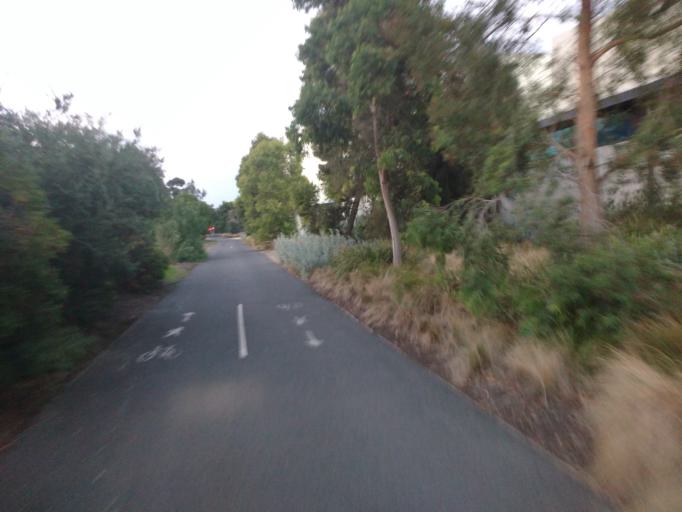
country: AU
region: Victoria
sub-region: Melbourne
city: West Melbourne
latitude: -37.8124
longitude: 144.9351
